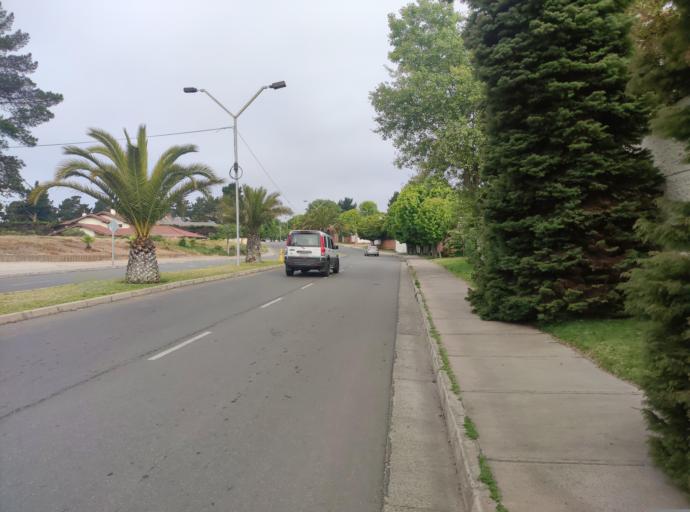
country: CL
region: Valparaiso
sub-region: Provincia de Valparaiso
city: Vina del Mar
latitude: -32.9432
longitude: -71.5400
